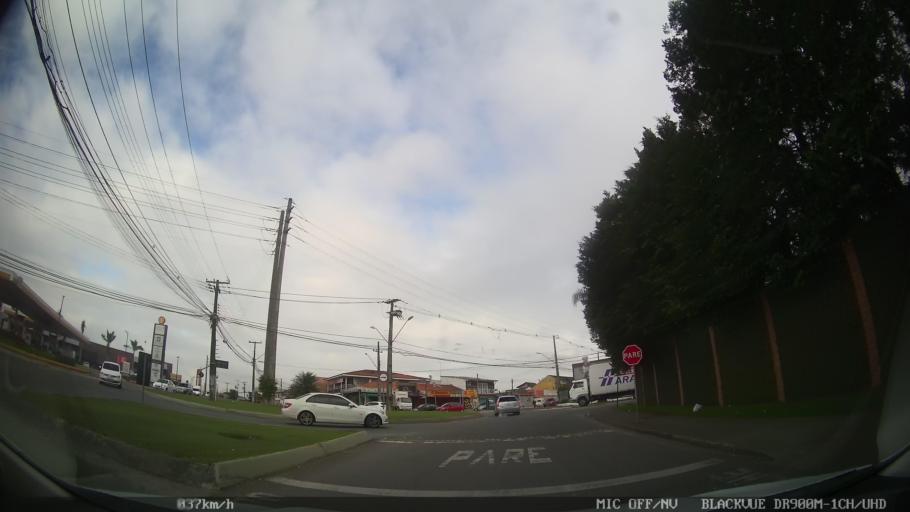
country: BR
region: Parana
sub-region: Curitiba
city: Curitiba
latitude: -25.3923
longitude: -49.3348
